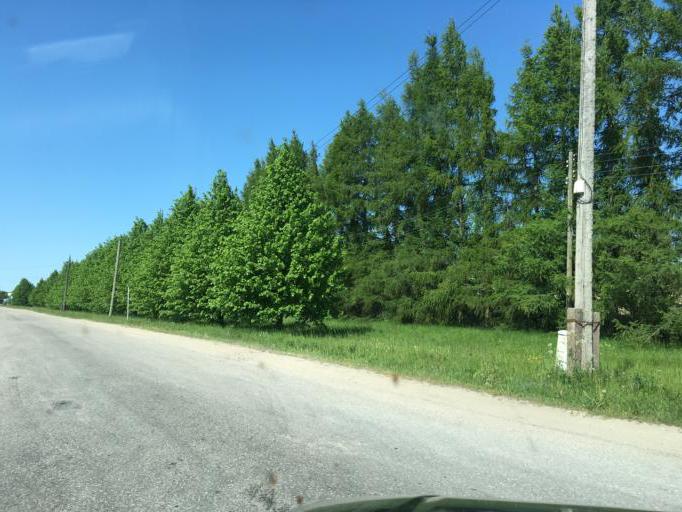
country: LV
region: Dundaga
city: Dundaga
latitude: 57.4999
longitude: 22.3530
